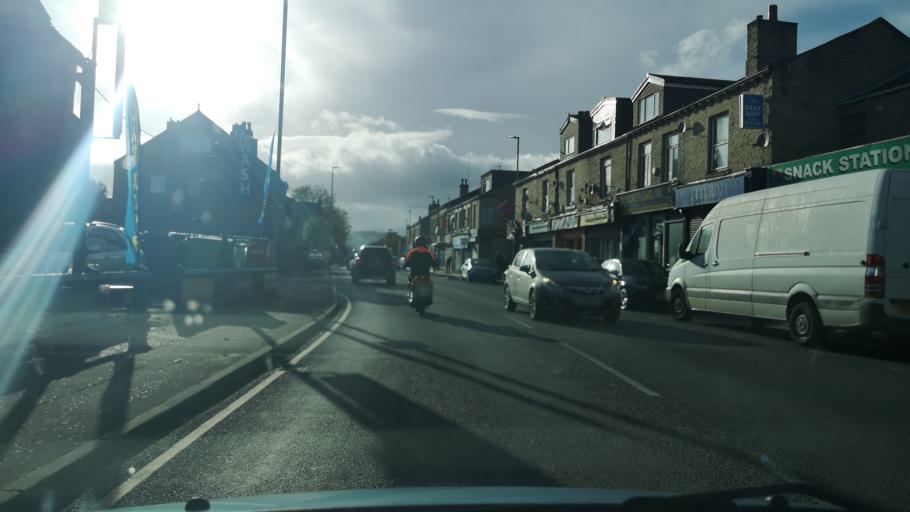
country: GB
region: England
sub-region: Kirklees
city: Heckmondwike
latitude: 53.6783
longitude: -1.6662
